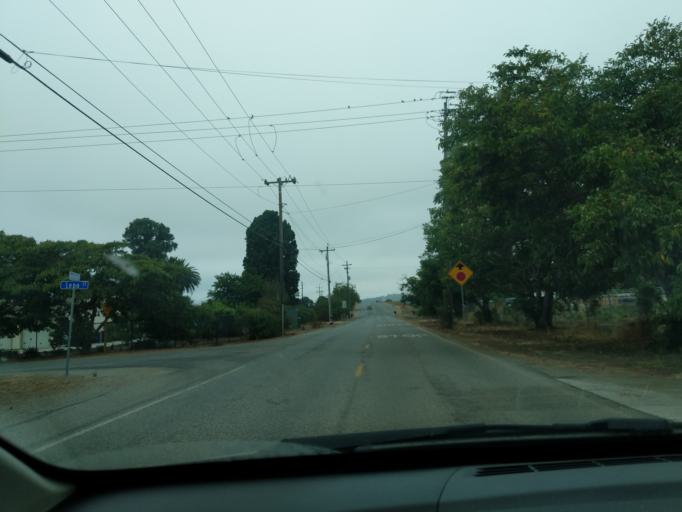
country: US
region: California
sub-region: Santa Clara County
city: Gilroy
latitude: 37.0449
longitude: -121.5733
